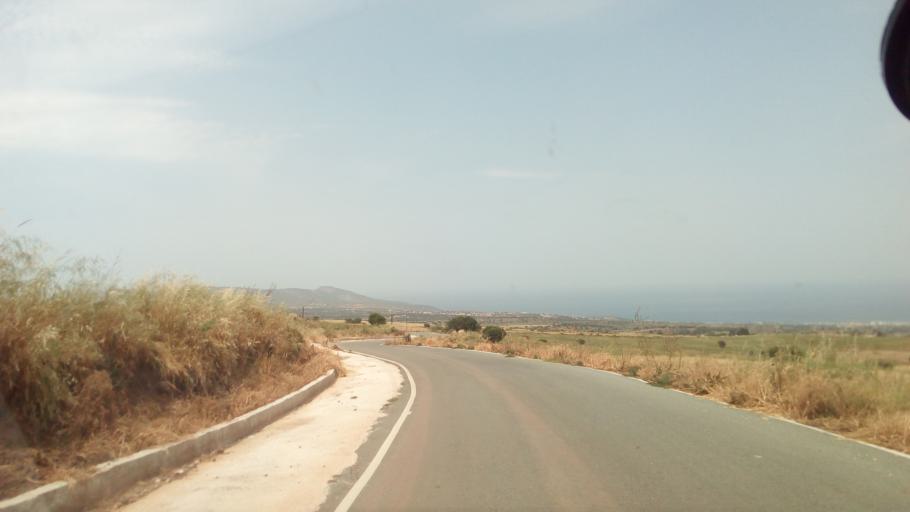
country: CY
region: Pafos
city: Polis
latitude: 34.9861
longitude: 32.3805
